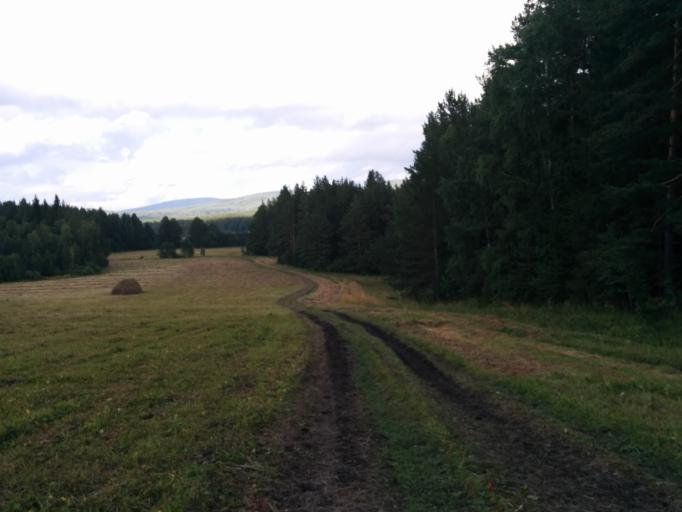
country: RU
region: Bashkortostan
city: Beloretsk
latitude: 54.0431
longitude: 58.3204
